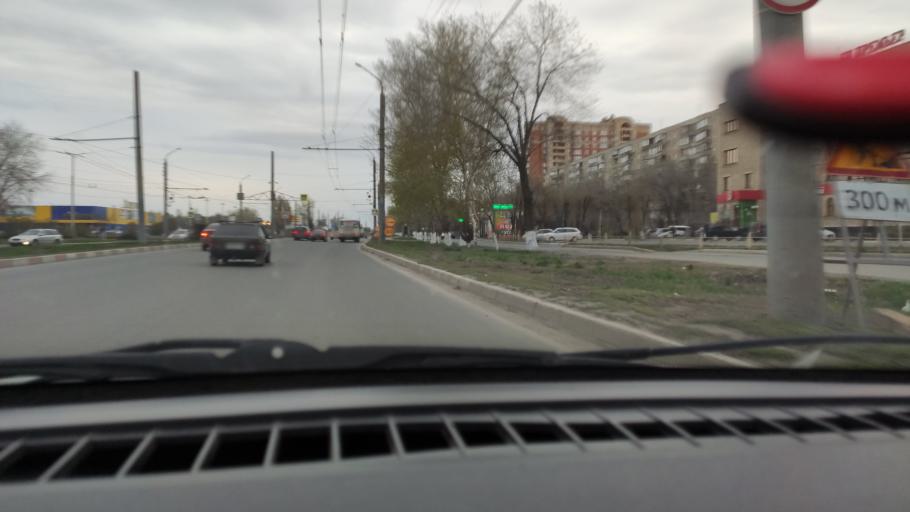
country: RU
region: Orenburg
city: Orenburg
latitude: 51.8159
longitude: 55.1073
